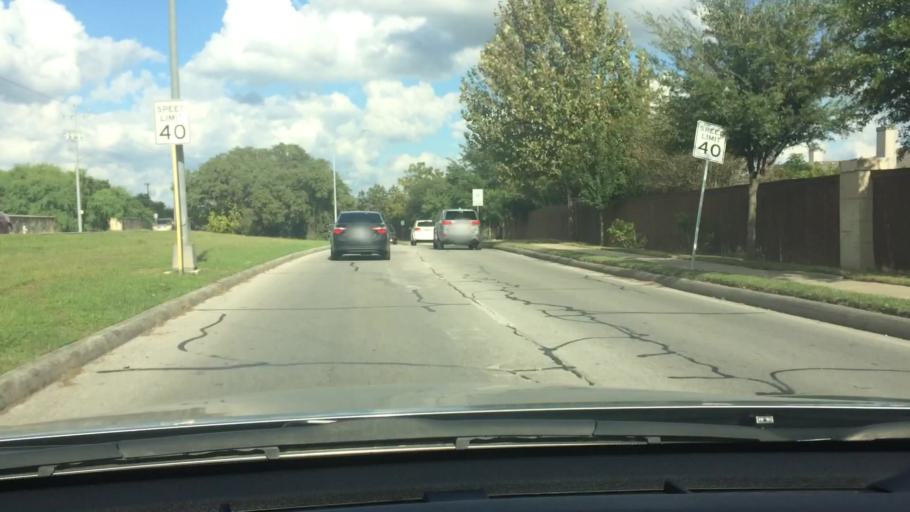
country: US
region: Texas
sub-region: Bexar County
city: Hollywood Park
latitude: 29.6389
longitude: -98.4434
